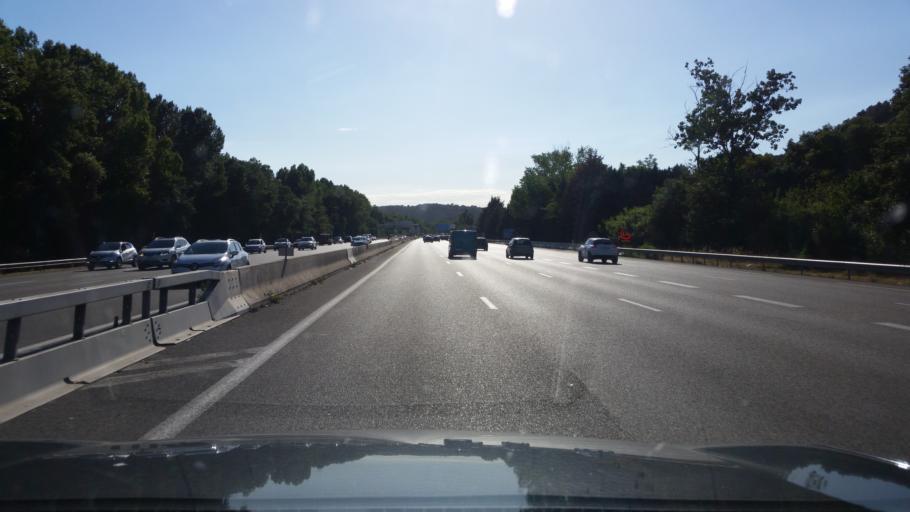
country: FR
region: Provence-Alpes-Cote d'Azur
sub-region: Departement des Bouches-du-Rhone
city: Chateauneuf-le-Rouge
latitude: 43.4817
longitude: 5.5541
